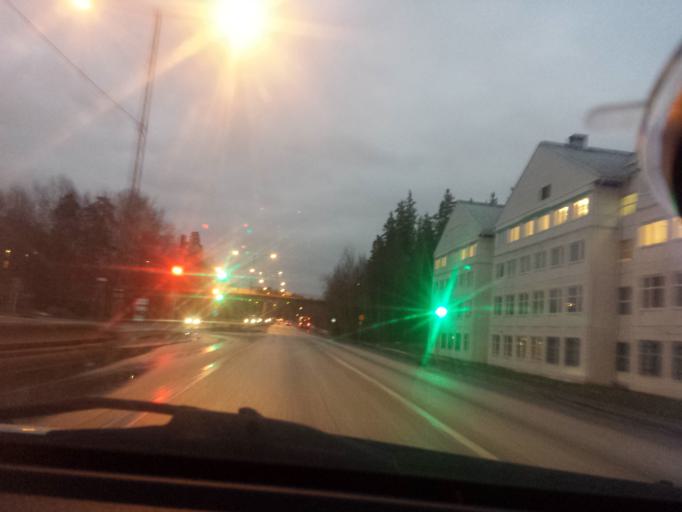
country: SE
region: Stockholm
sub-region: Stockholms Kommun
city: Kista
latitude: 59.4165
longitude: 17.9238
